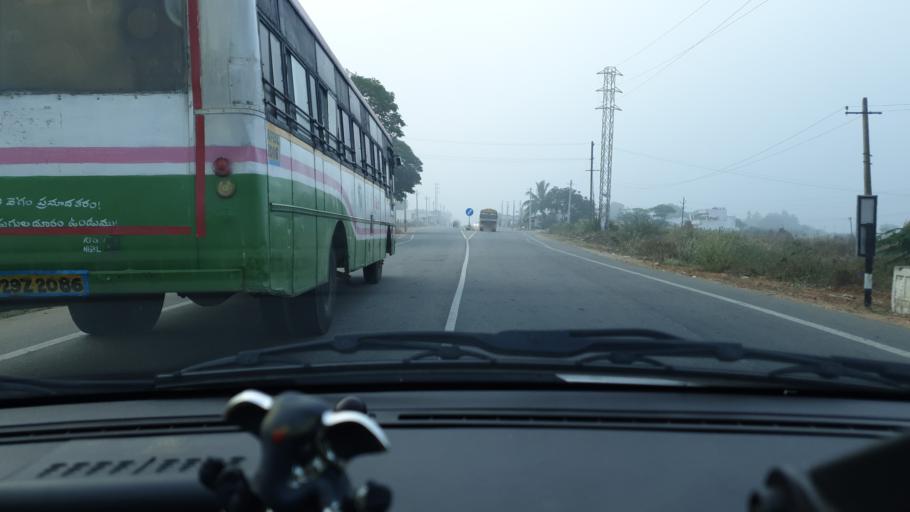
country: IN
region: Telangana
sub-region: Mahbubnagar
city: Farrukhnagar
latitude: 16.8860
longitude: 78.5290
